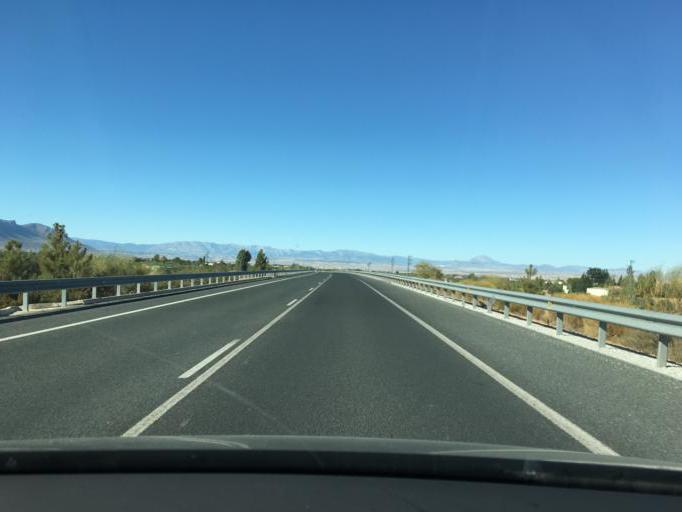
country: ES
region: Andalusia
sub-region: Provincia de Granada
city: Caniles
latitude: 37.4639
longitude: -2.7371
